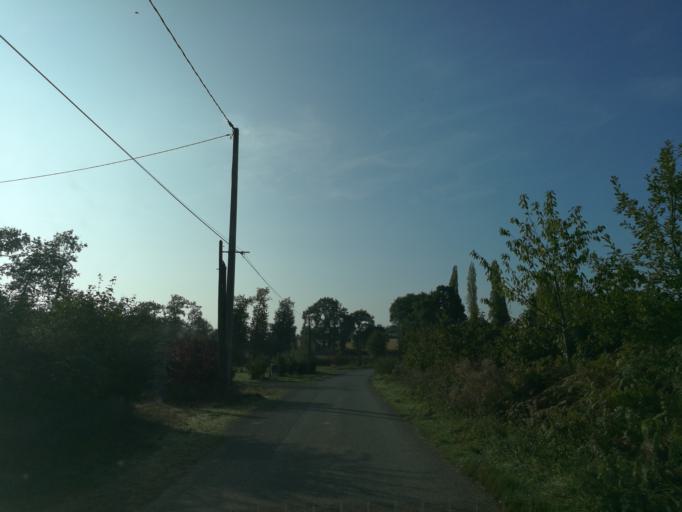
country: FR
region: Brittany
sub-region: Departement d'Ille-et-Vilaine
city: Pleumeleuc
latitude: 48.1684
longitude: -1.9113
